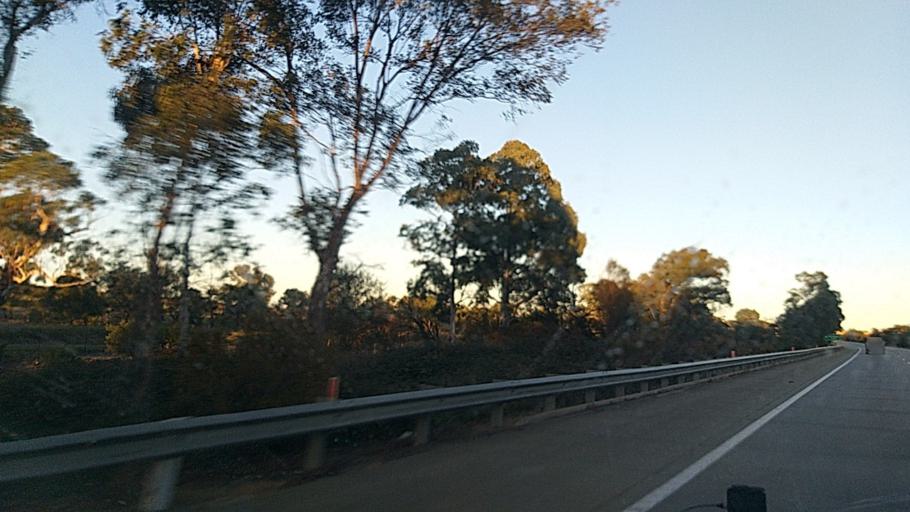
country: AU
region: New South Wales
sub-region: Goulburn Mulwaree
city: Goulburn
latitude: -34.7761
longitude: 149.6957
